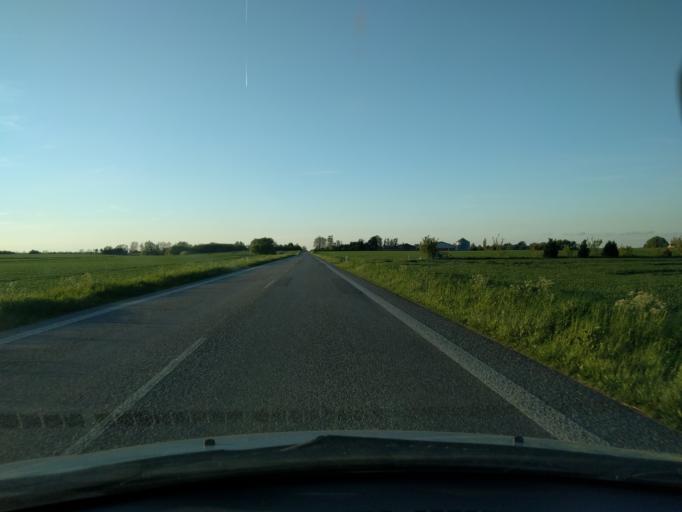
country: DK
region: Zealand
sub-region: Guldborgsund Kommune
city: Stubbekobing
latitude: 54.8252
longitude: 11.9948
